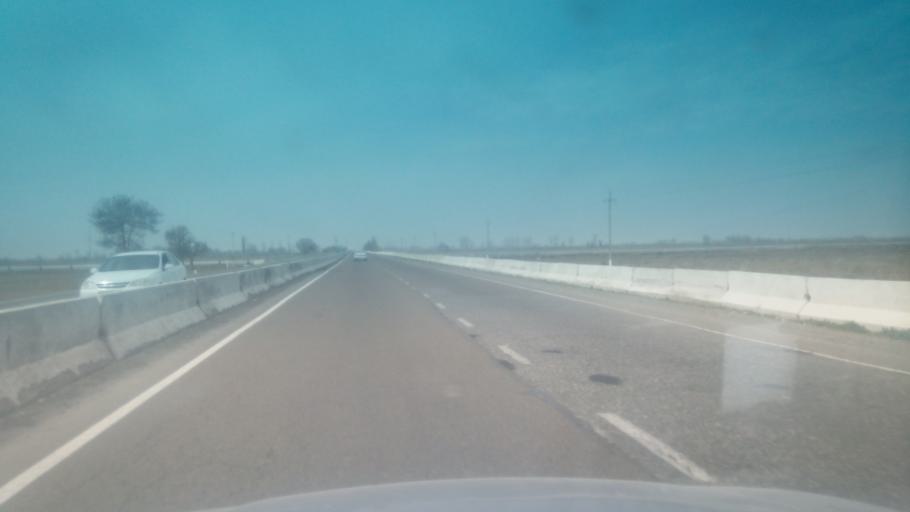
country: KZ
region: Ongtustik Qazaqstan
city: Myrzakent
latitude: 40.5206
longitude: 68.4654
